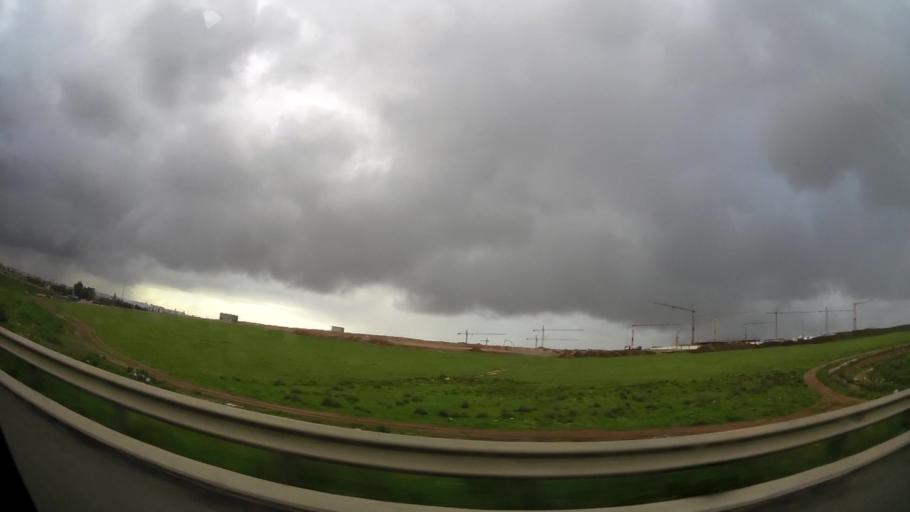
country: MA
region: Grand Casablanca
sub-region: Mediouna
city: Tit Mellil
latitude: 33.5660
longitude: -7.4803
